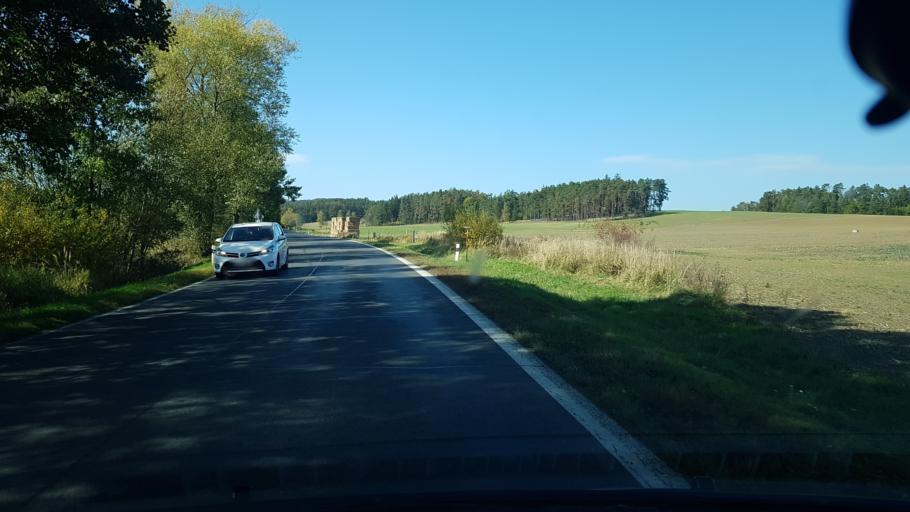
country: CZ
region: Jihocesky
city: Radomysl
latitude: 49.2954
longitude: 14.0260
